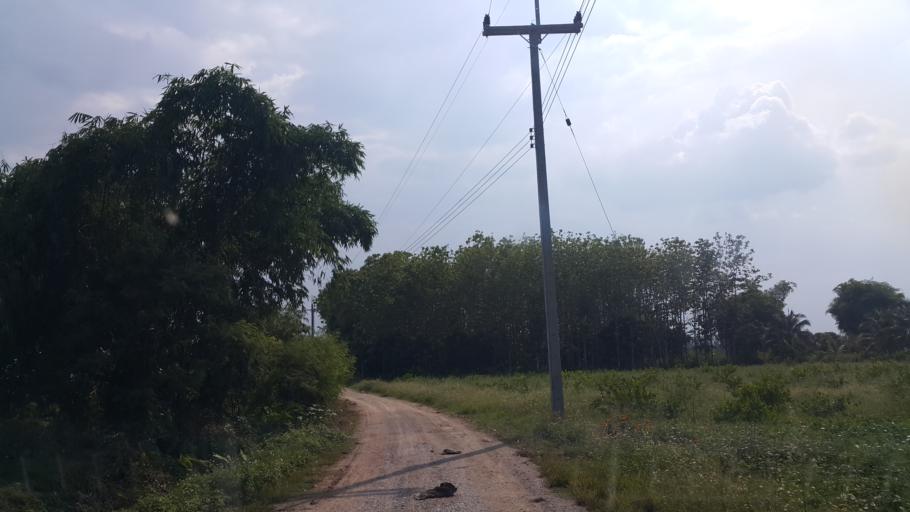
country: TH
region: Chiang Rai
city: Wiang Chai
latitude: 19.9148
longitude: 99.9134
